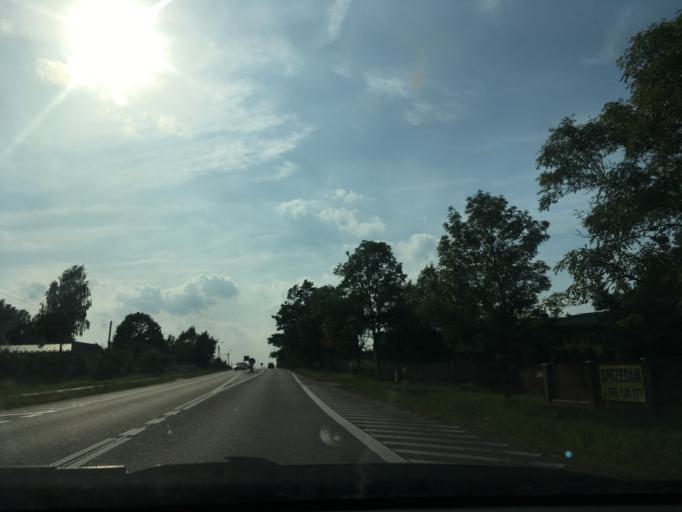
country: PL
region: Podlasie
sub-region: Powiat bialostocki
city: Wasilkow
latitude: 53.1253
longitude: 23.2650
